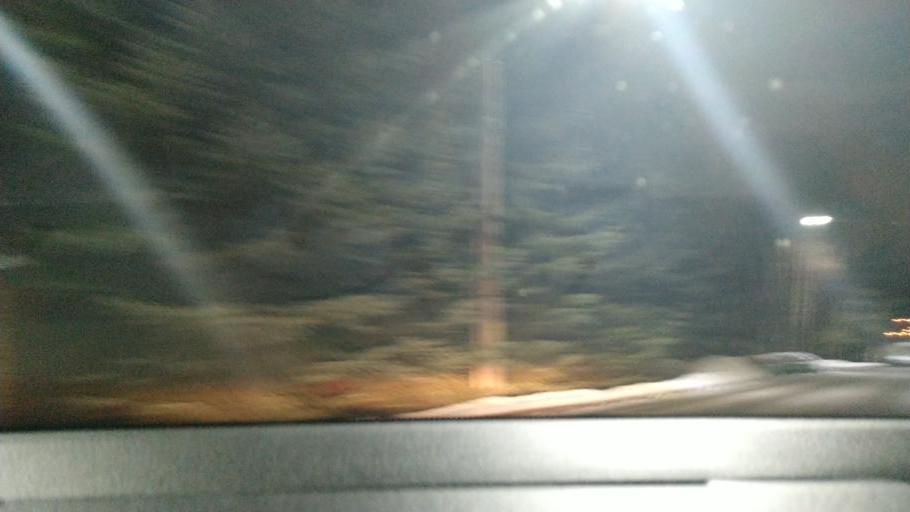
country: RU
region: Moskovskaya
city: Barvikha
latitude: 55.7160
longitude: 37.2831
